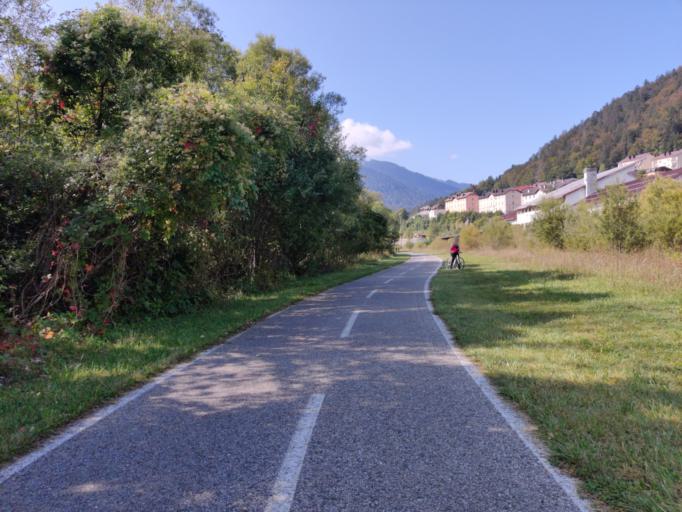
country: IT
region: Friuli Venezia Giulia
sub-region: Provincia di Udine
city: Tarvisio
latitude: 46.5112
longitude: 13.6061
